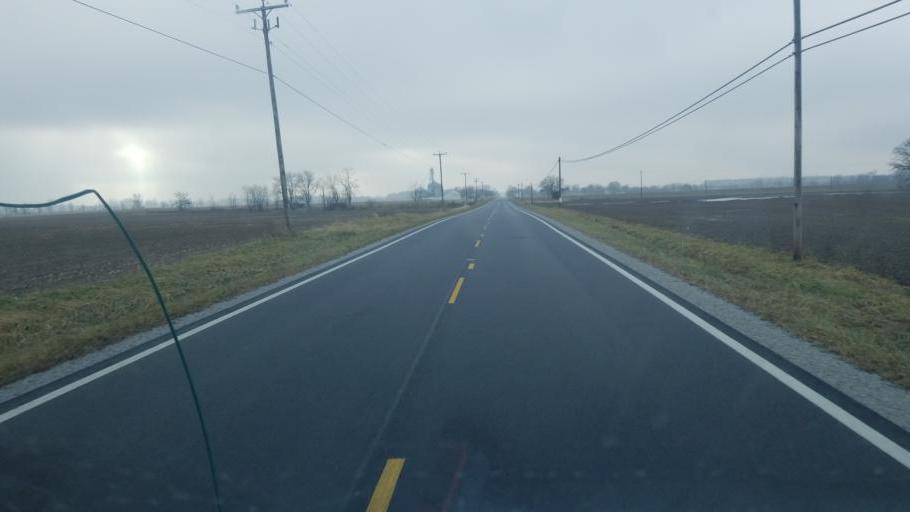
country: US
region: Ohio
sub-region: Hardin County
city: Kenton
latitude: 40.6724
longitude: -83.5347
